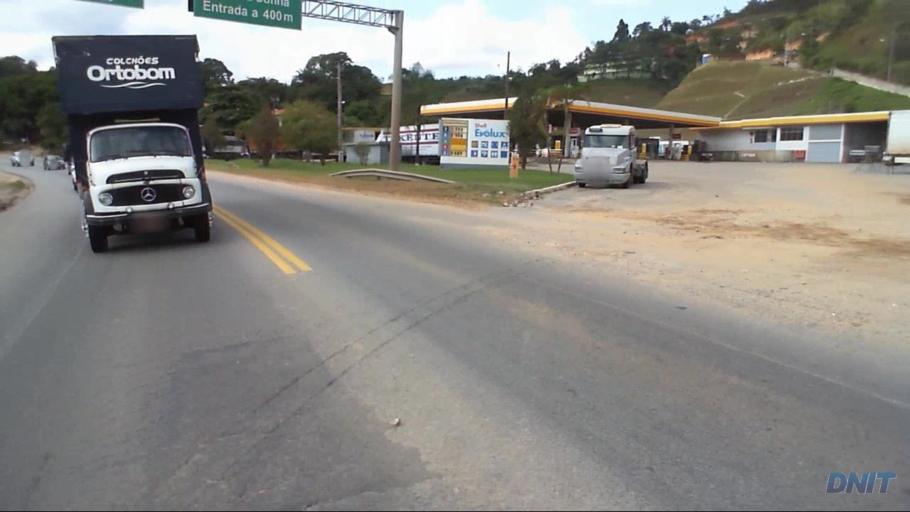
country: BR
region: Minas Gerais
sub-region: Santa Luzia
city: Santa Luzia
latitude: -19.8413
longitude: -43.8618
